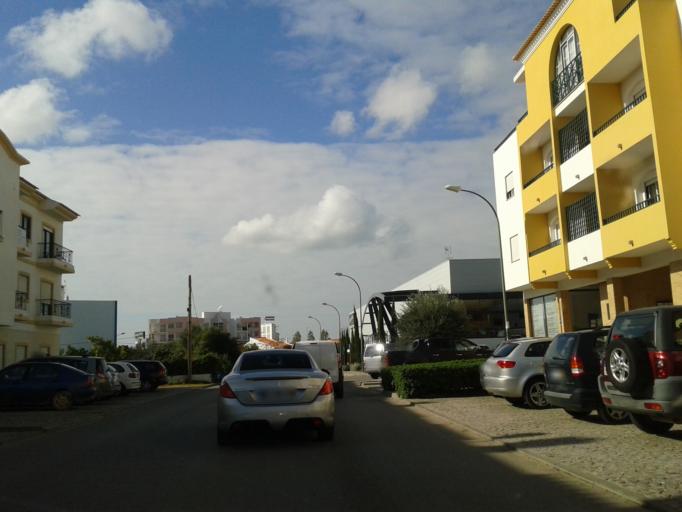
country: PT
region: Faro
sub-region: Loule
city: Almancil
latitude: 37.0895
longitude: -8.0330
